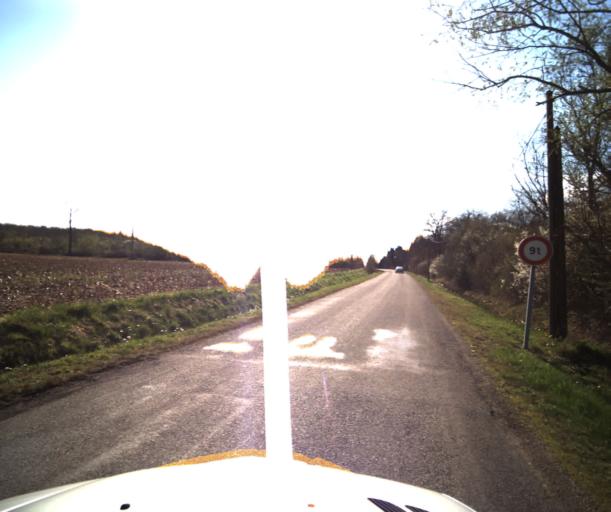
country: FR
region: Midi-Pyrenees
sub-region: Departement du Tarn-et-Garonne
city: Bressols
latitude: 43.9578
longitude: 1.2866
